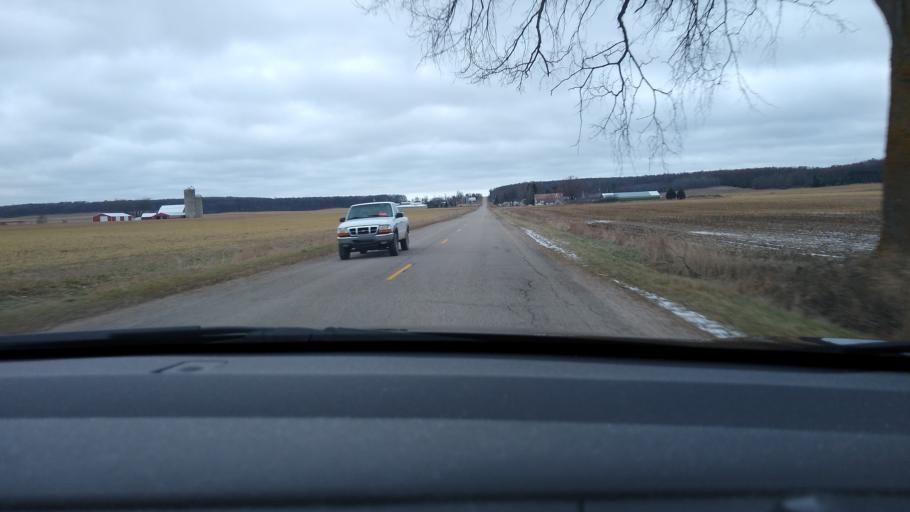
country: US
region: Michigan
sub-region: Missaukee County
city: Lake City
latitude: 44.2740
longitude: -85.0540
